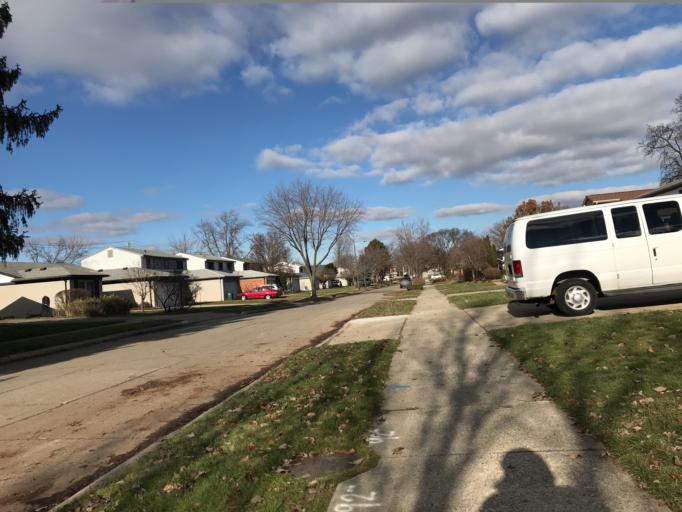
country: US
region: Michigan
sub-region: Oakland County
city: Southfield
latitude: 42.4835
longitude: -83.1991
